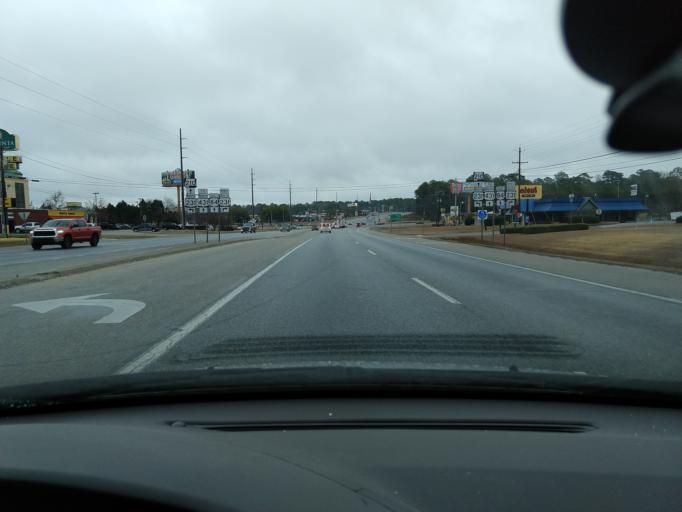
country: US
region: Alabama
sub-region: Houston County
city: Dothan
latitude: 31.2473
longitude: -85.4266
